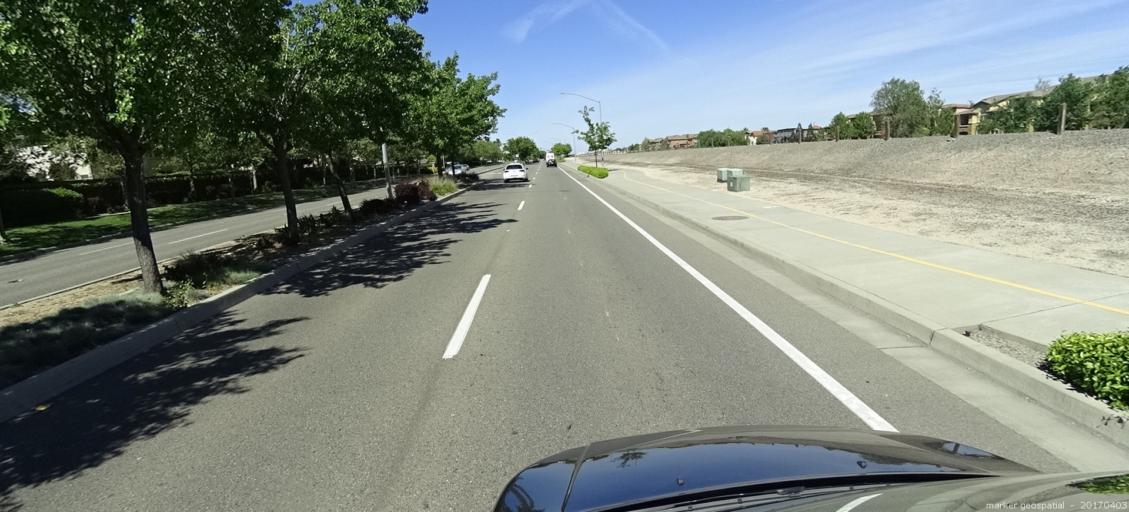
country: US
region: California
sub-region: Sacramento County
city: Rio Linda
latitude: 38.6677
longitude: -121.5077
